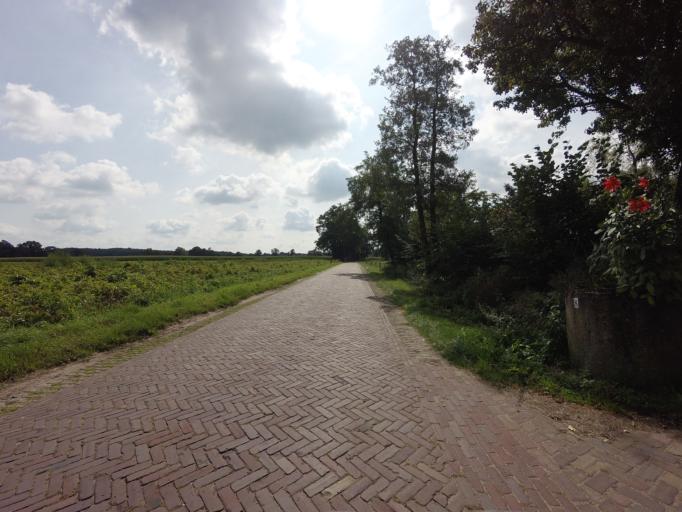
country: DE
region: Lower Saxony
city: Getelo
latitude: 52.4426
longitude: 6.8285
